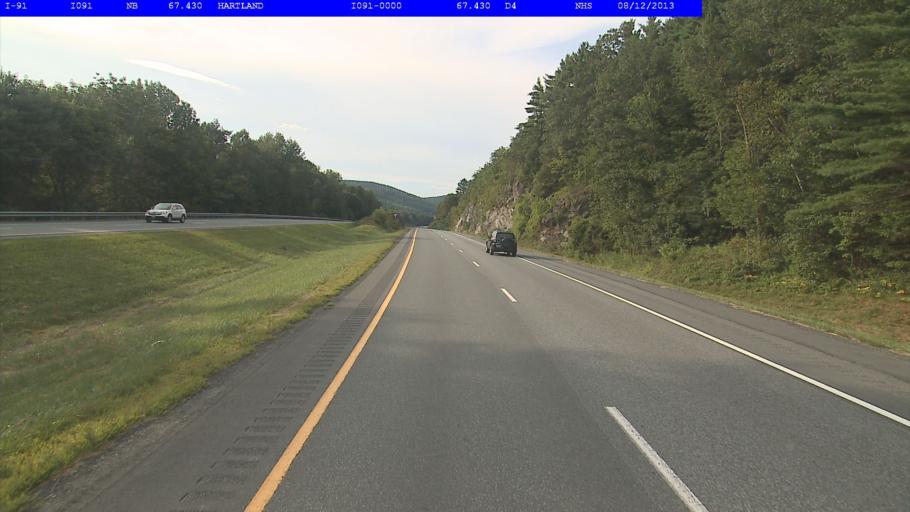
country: US
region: Vermont
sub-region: Windsor County
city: White River Junction
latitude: 43.6073
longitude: -72.3421
